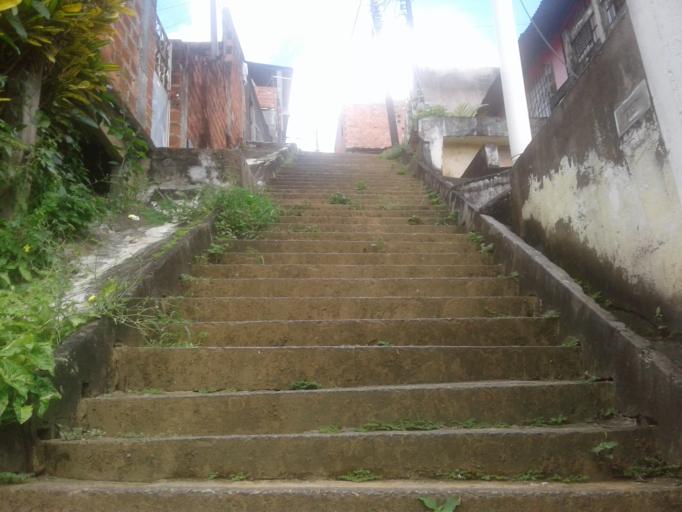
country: BR
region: Bahia
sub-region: Salvador
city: Salvador
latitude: -12.9094
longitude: -38.4741
